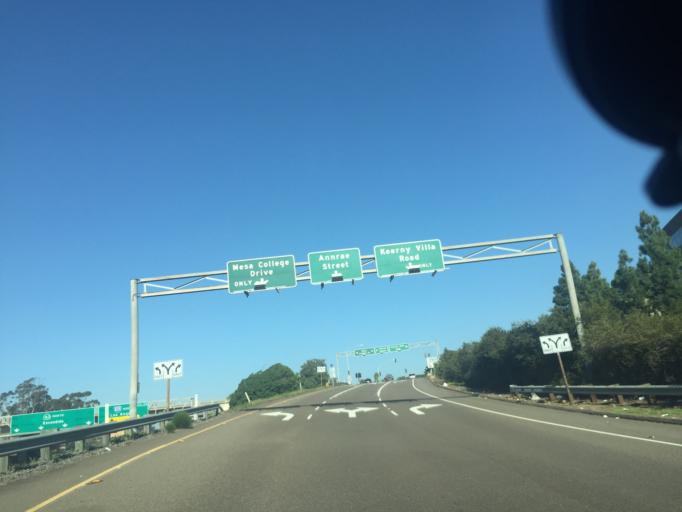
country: US
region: California
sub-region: San Diego County
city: San Diego
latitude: 32.8007
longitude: -117.1554
